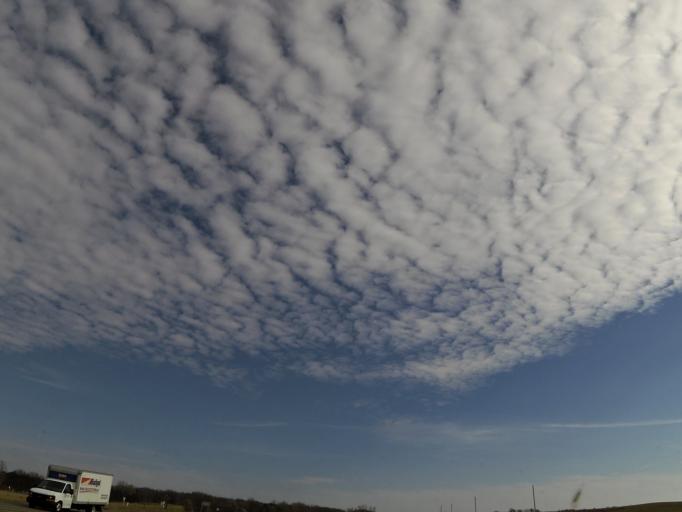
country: US
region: Minnesota
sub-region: Steele County
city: Medford
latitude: 44.2047
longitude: -93.2600
